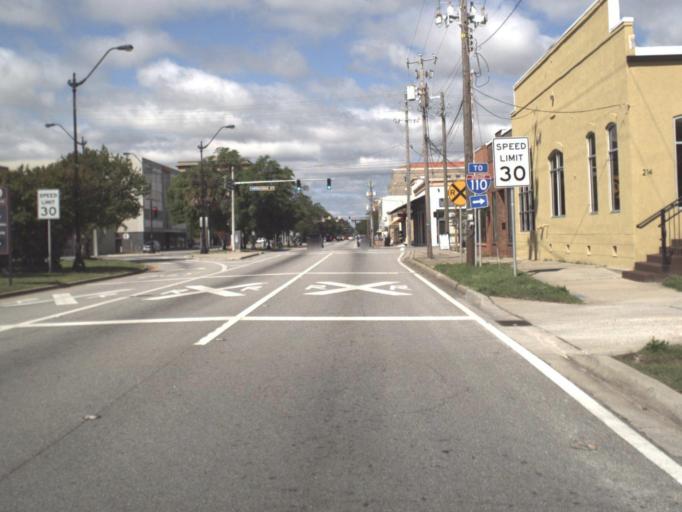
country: US
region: Florida
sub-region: Escambia County
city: Pensacola
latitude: 30.4137
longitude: -87.2120
